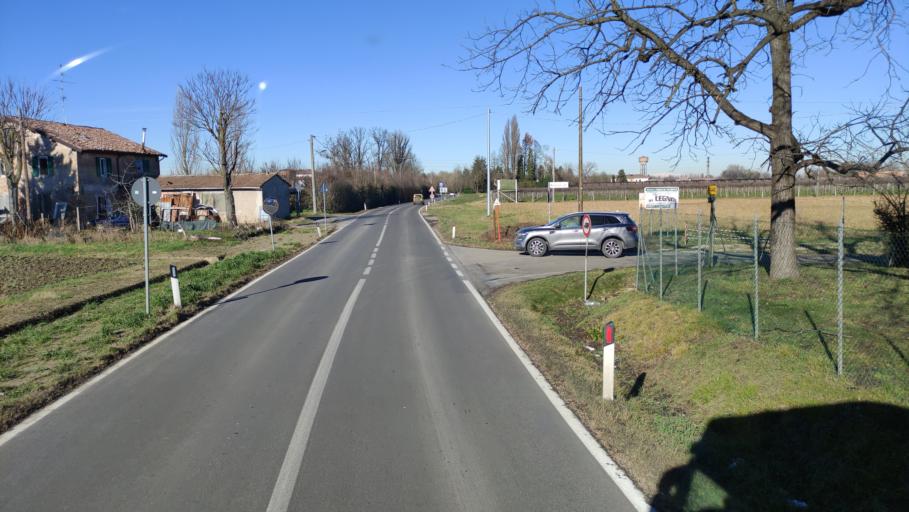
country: IT
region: Emilia-Romagna
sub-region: Provincia di Reggio Emilia
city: Correggio
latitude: 44.7835
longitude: 10.7782
